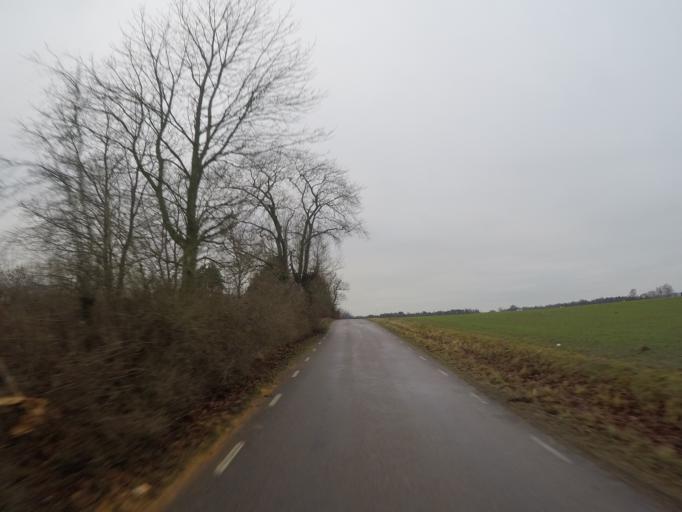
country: SE
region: Skane
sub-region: Hoors Kommun
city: Loberod
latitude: 55.7458
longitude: 13.4124
